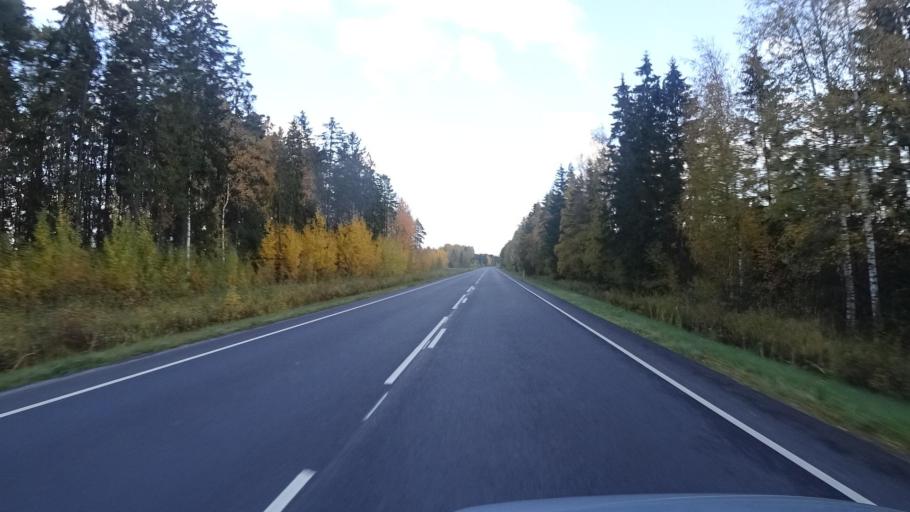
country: FI
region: Satakunta
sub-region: Rauma
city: Koeylioe
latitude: 61.0870
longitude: 22.2567
